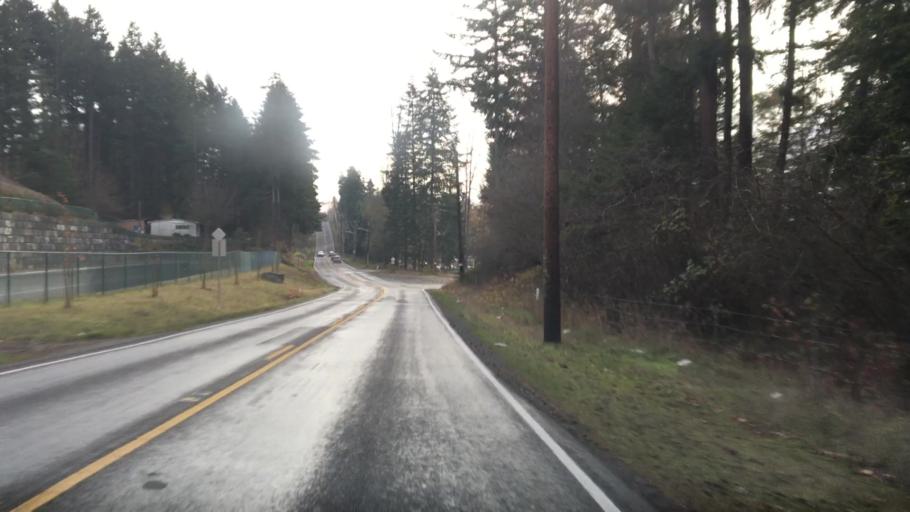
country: US
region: Washington
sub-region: Pierce County
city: Frederickson
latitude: 47.1162
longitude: -122.3254
